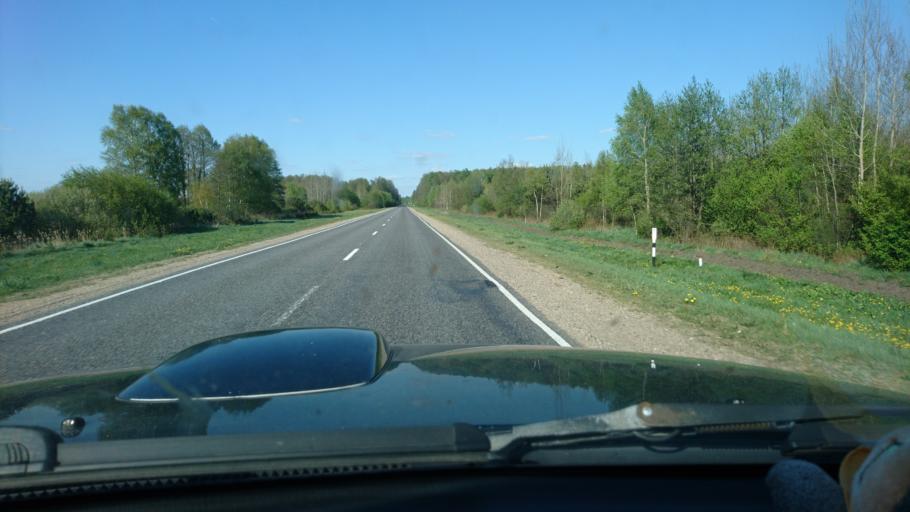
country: BY
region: Brest
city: Zhabinka
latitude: 52.3910
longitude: 24.1705
